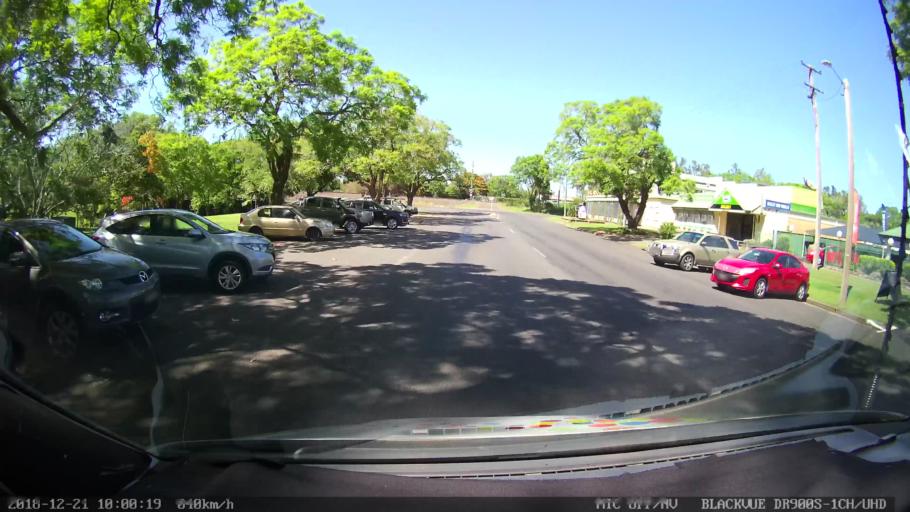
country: AU
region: New South Wales
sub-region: Clarence Valley
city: Grafton
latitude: -29.6834
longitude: 152.9267
